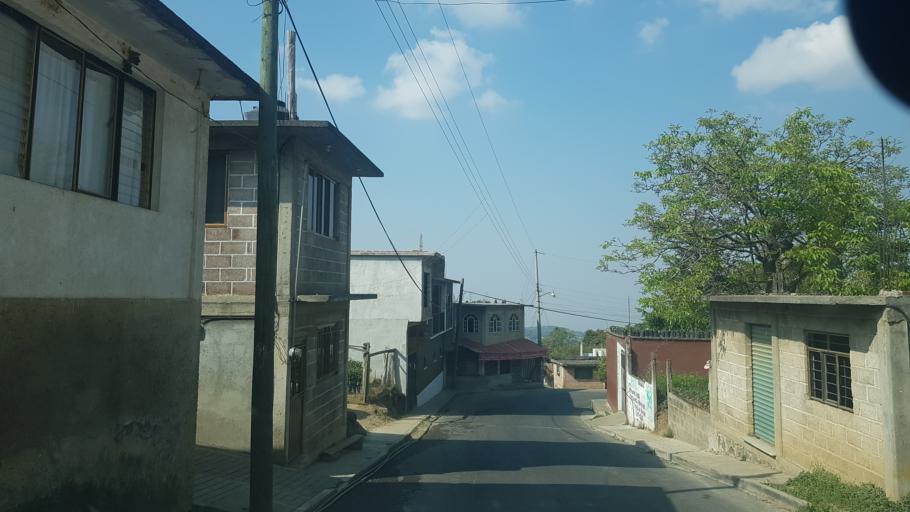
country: MX
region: Morelos
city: Hueyapan
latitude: 18.8928
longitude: -98.6759
